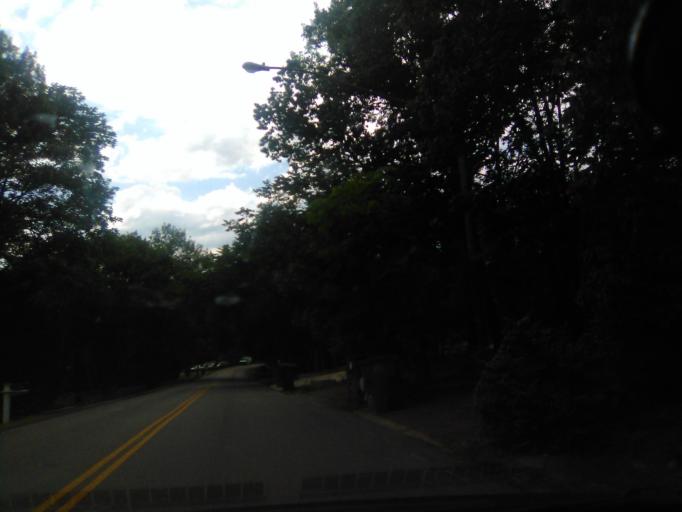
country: US
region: Tennessee
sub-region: Davidson County
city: Belle Meade
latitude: 36.1314
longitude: -86.8750
